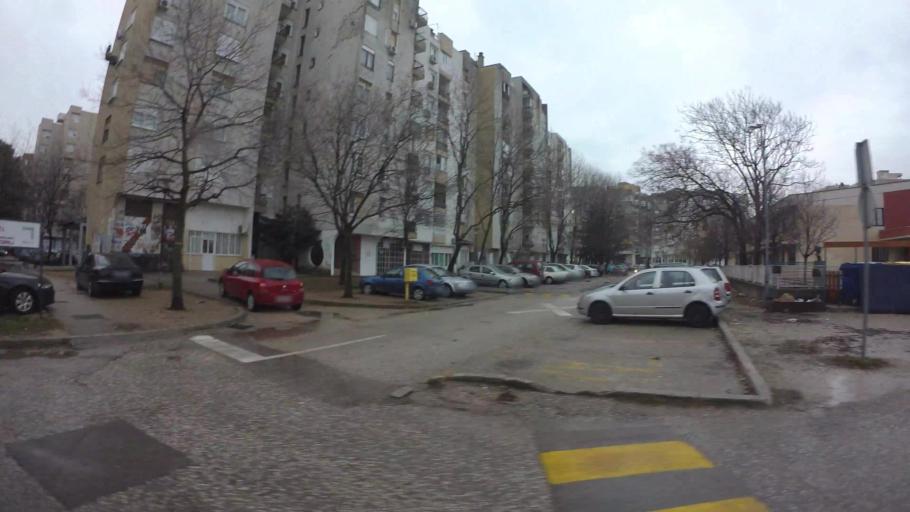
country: BA
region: Federation of Bosnia and Herzegovina
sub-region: Hercegovacko-Bosanski Kanton
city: Mostar
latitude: 43.3522
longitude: 17.8046
